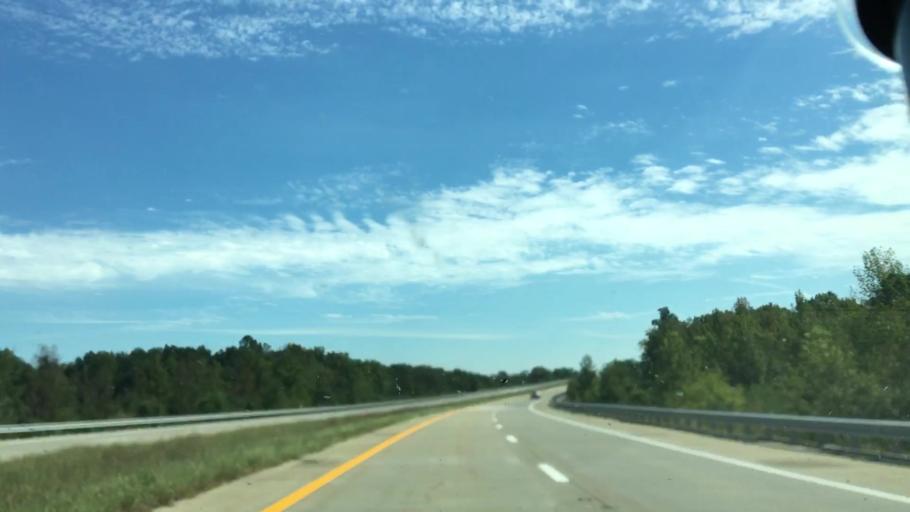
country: US
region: Kentucky
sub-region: Daviess County
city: Owensboro
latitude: 37.7612
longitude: -87.3030
